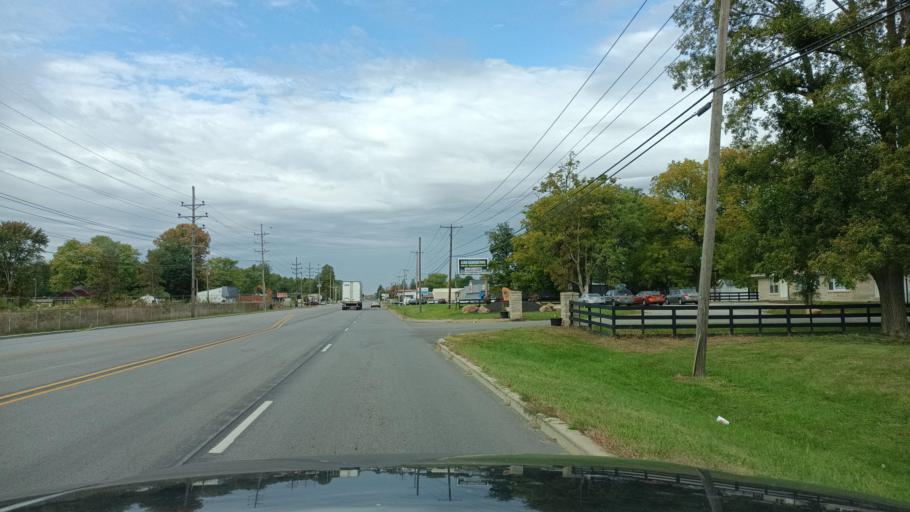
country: US
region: Indiana
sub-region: Delaware County
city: Yorktown
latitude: 40.1811
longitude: -85.4503
